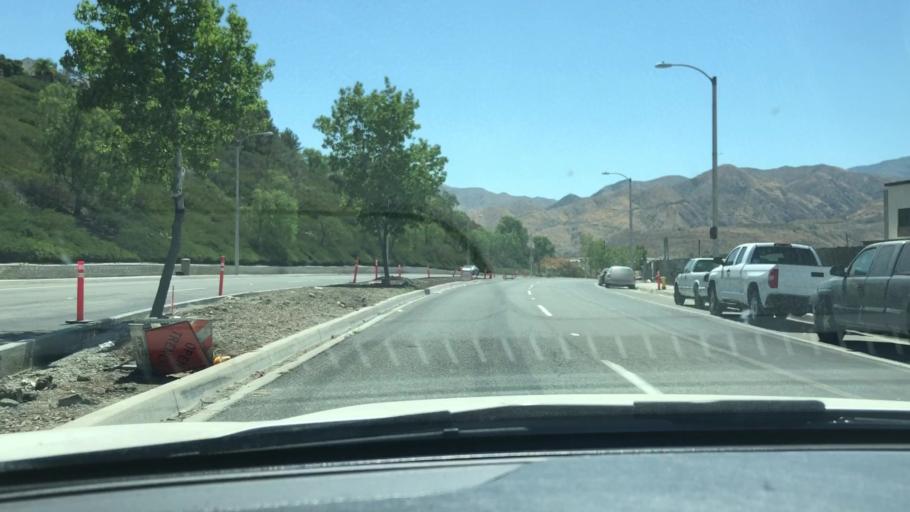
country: US
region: California
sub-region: Los Angeles County
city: Agua Dulce
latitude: 34.4354
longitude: -118.3889
